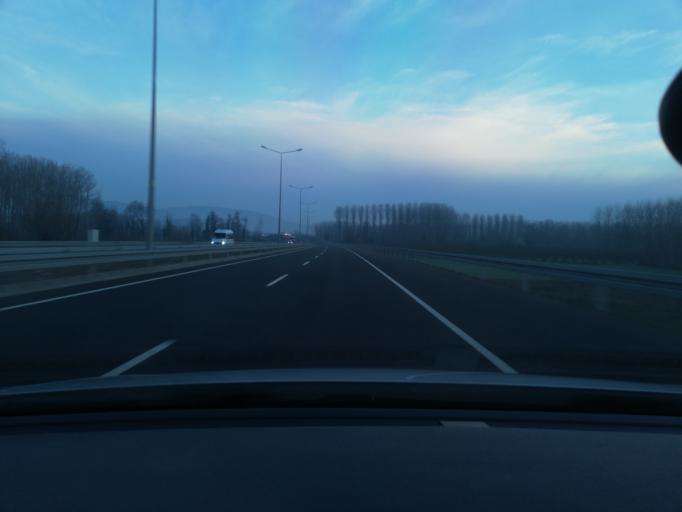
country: TR
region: Duzce
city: Duzce
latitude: 40.8114
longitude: 31.1692
